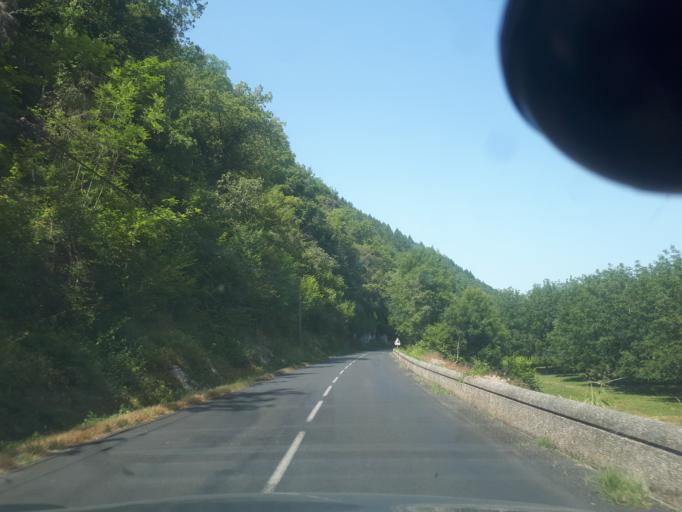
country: FR
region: Midi-Pyrenees
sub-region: Departement du Lot
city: Souillac
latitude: 44.8643
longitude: 1.4315
